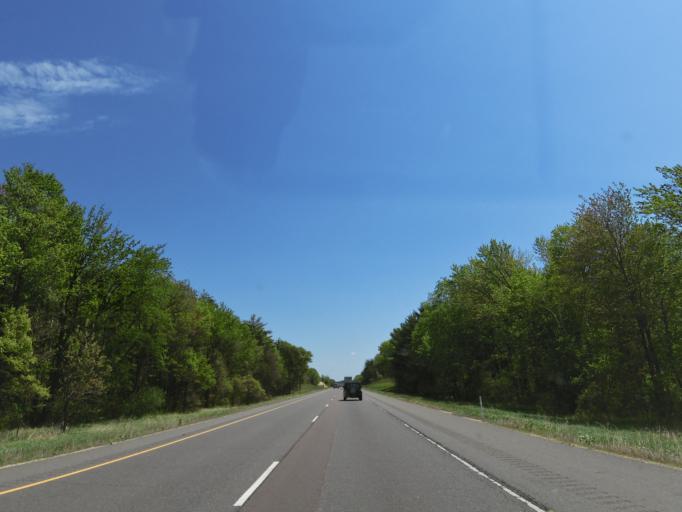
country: US
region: Wisconsin
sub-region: Juneau County
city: New Lisbon
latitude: 43.9462
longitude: -90.3252
